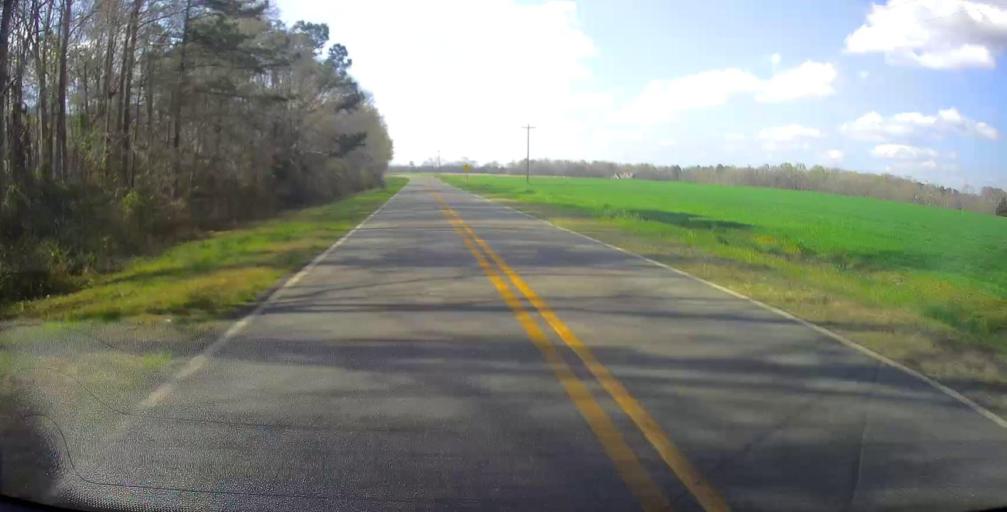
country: US
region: Georgia
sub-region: Wilkinson County
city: Irwinton
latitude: 32.6310
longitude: -83.1008
